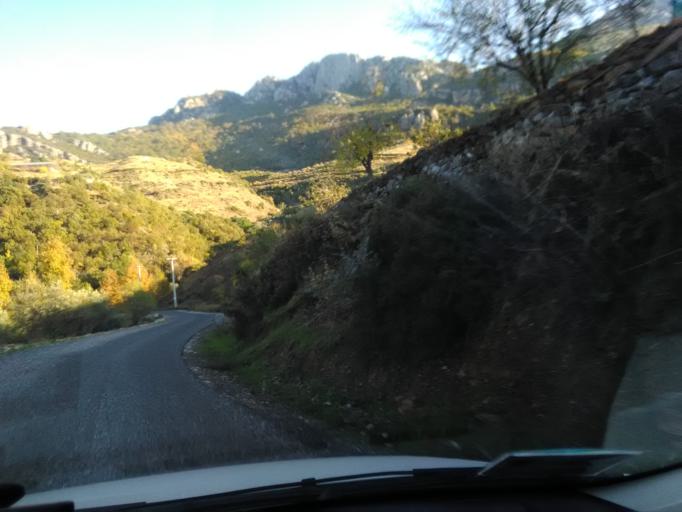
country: TR
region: Antalya
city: Gazipasa
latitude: 36.3087
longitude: 32.4075
